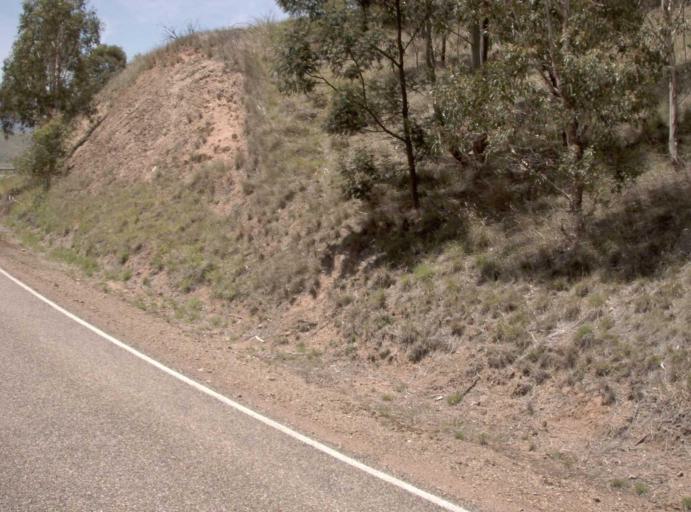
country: AU
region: Victoria
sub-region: Alpine
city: Mount Beauty
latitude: -37.1634
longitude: 147.6647
